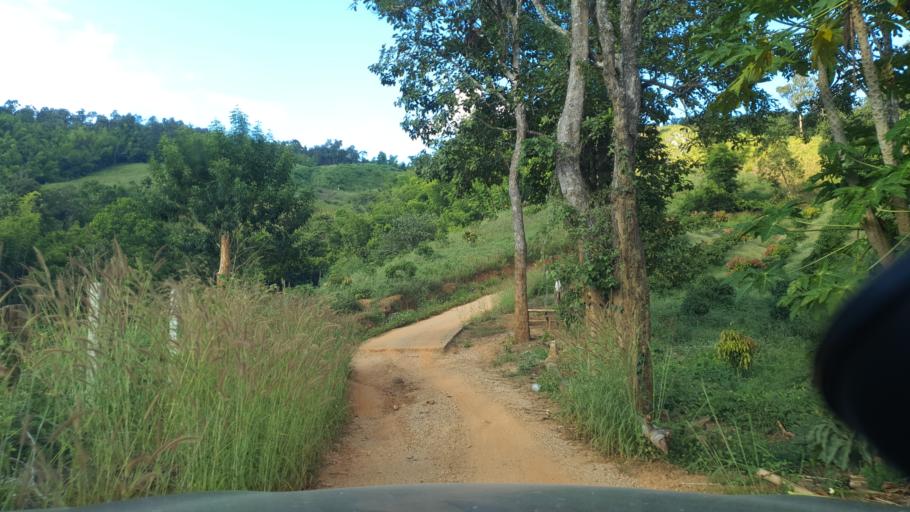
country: TH
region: Chiang Mai
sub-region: Amphoe Chiang Dao
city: Chiang Dao
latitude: 19.4051
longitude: 98.8312
